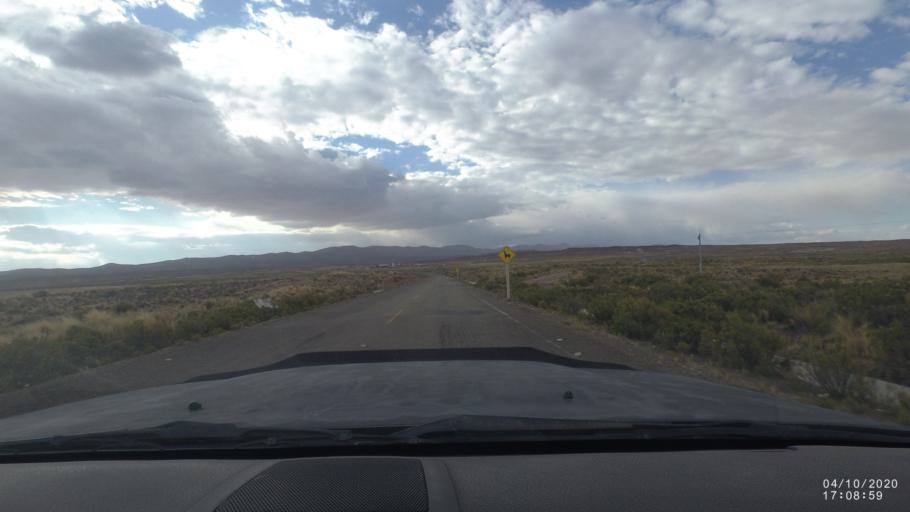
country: BO
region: Oruro
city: Oruro
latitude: -18.3433
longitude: -67.5781
